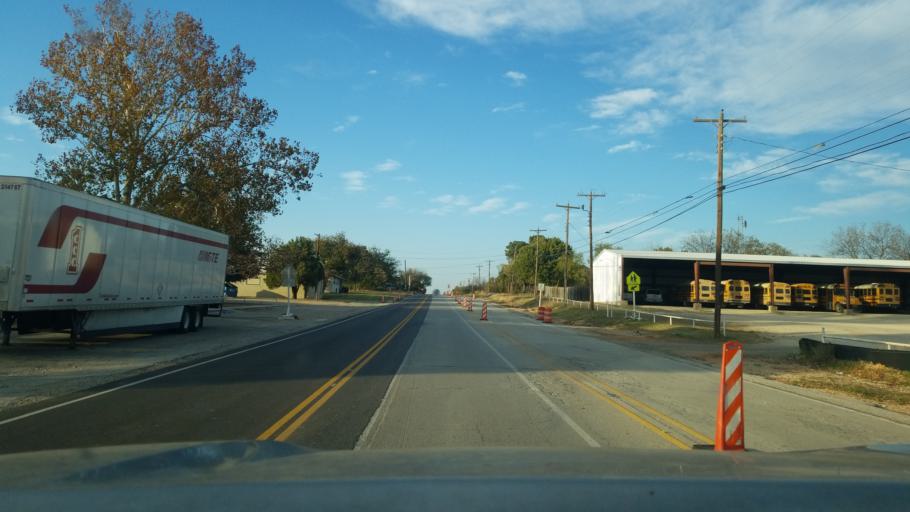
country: US
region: Texas
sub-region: Brown County
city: Lake Brownwood
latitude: 32.1048
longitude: -98.9643
